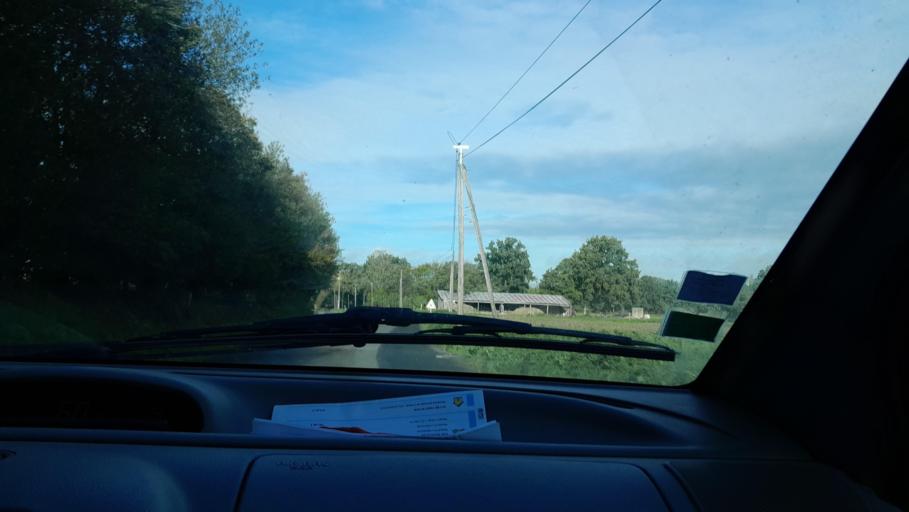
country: FR
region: Lower Normandy
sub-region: Departement de la Manche
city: Pontorson
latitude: 48.5576
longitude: -1.4589
